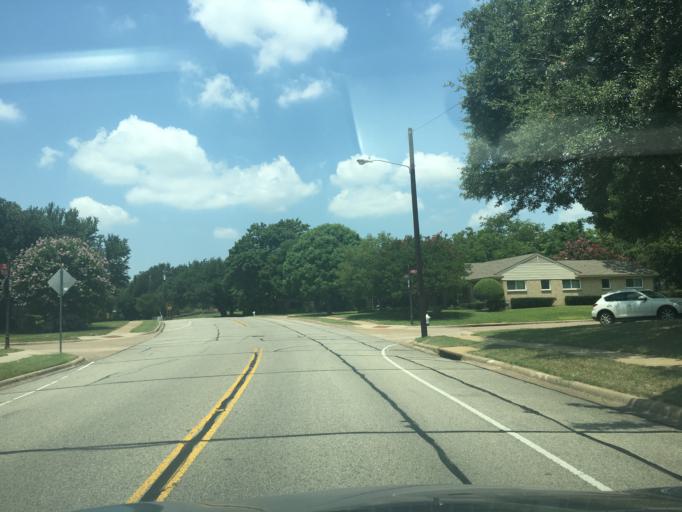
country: US
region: Texas
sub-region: Dallas County
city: Carrollton
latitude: 32.9436
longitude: -96.8689
